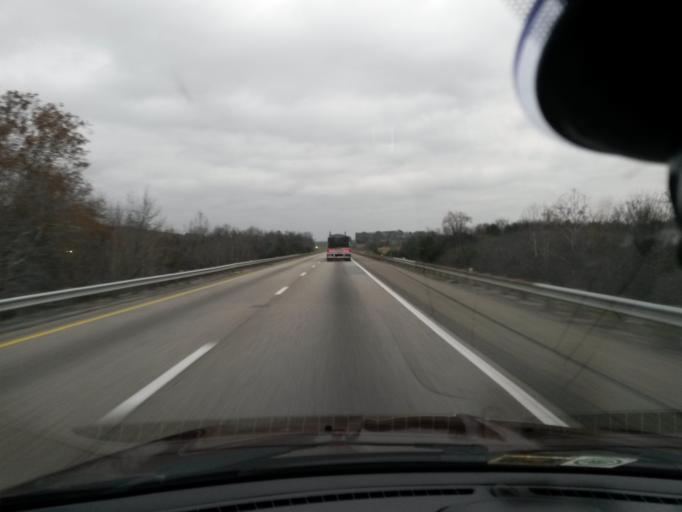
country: US
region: Virginia
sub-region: Augusta County
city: Jolivue
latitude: 38.0673
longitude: -79.1020
